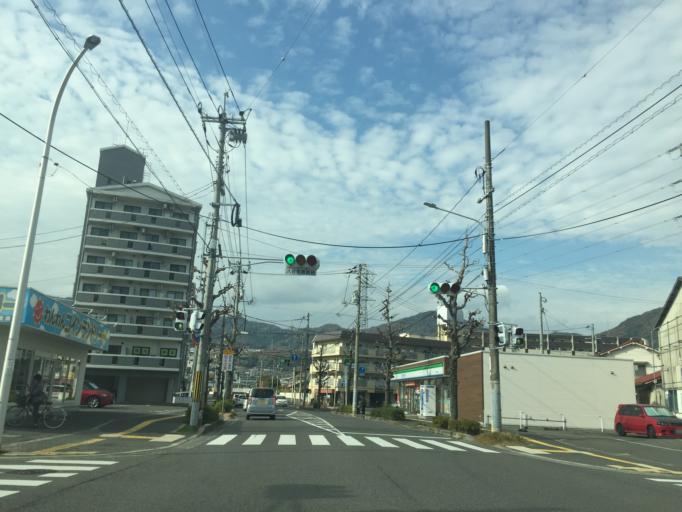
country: JP
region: Hiroshima
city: Hiroshima-shi
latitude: 34.4340
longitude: 132.4612
